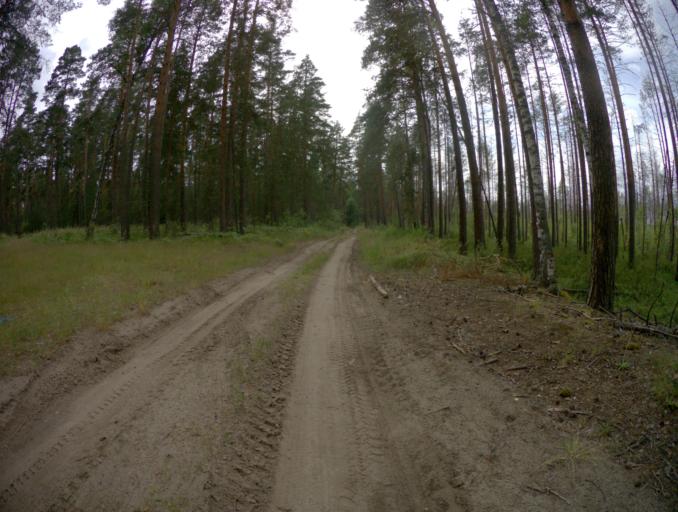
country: RU
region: Vladimir
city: Gorokhovets
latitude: 56.3000
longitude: 42.6783
